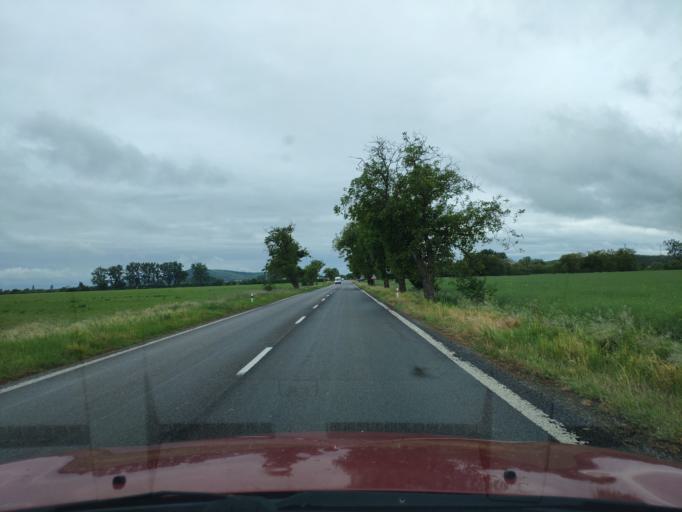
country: HU
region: Borsod-Abauj-Zemplen
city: Karcsa
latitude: 48.4156
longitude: 21.8290
